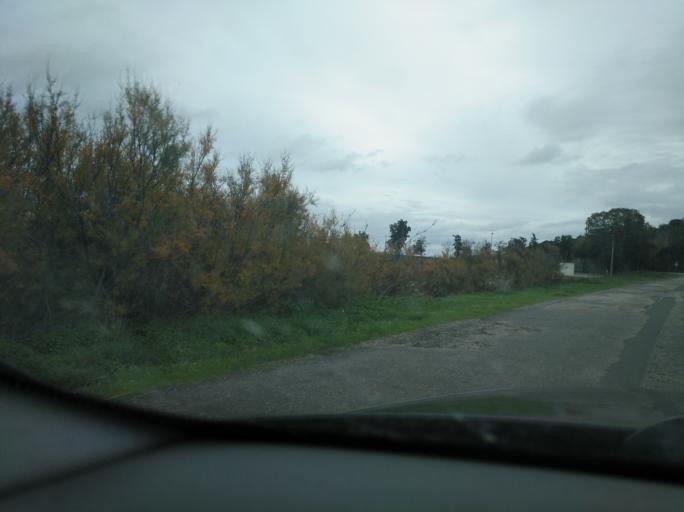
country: PT
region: Faro
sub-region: Vila Real de Santo Antonio
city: Monte Gordo
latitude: 37.1967
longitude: -7.4866
